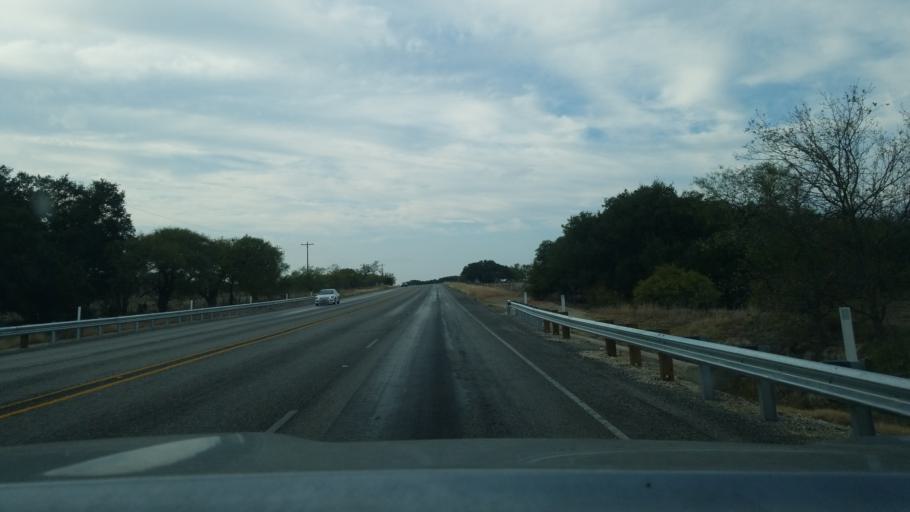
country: US
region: Texas
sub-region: Mills County
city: Goldthwaite
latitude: 31.5435
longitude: -98.6297
